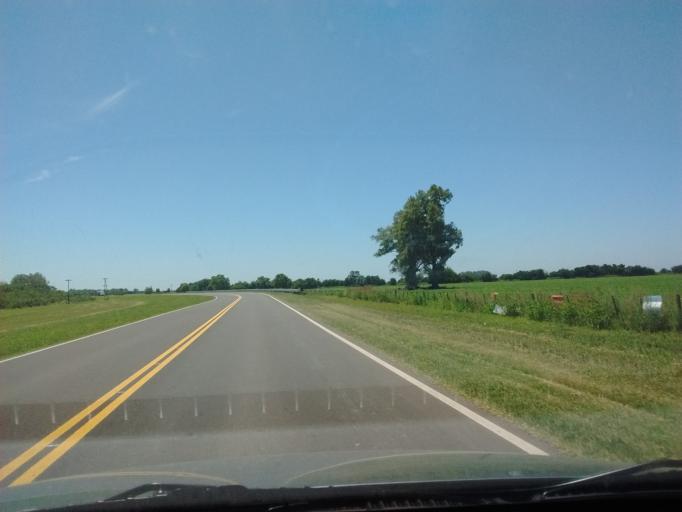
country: AR
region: Entre Rios
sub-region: Departamento de Victoria
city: Victoria
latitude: -32.8535
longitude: -59.8506
